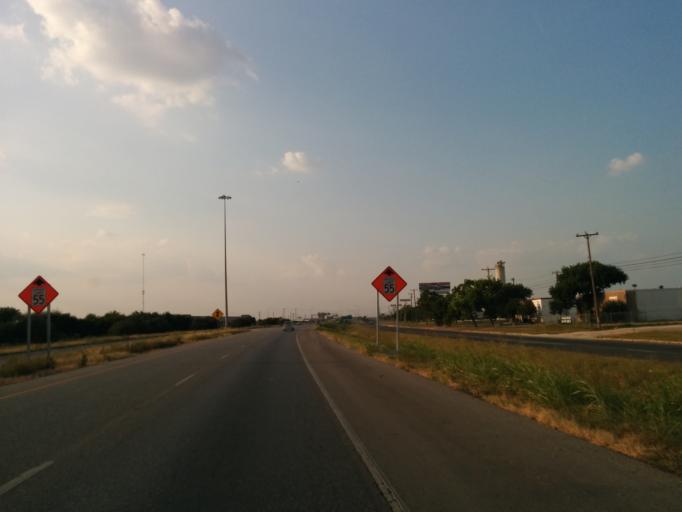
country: US
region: Texas
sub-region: Bexar County
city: Kirby
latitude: 29.4521
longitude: -98.4038
